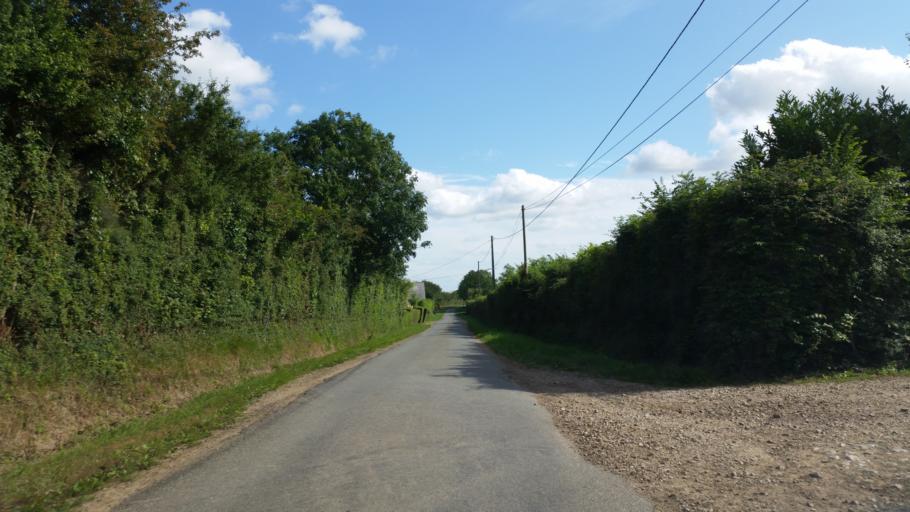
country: FR
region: Lower Normandy
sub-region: Departement de la Manche
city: Sainte-Mere-Eglise
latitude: 49.4571
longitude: -1.2925
